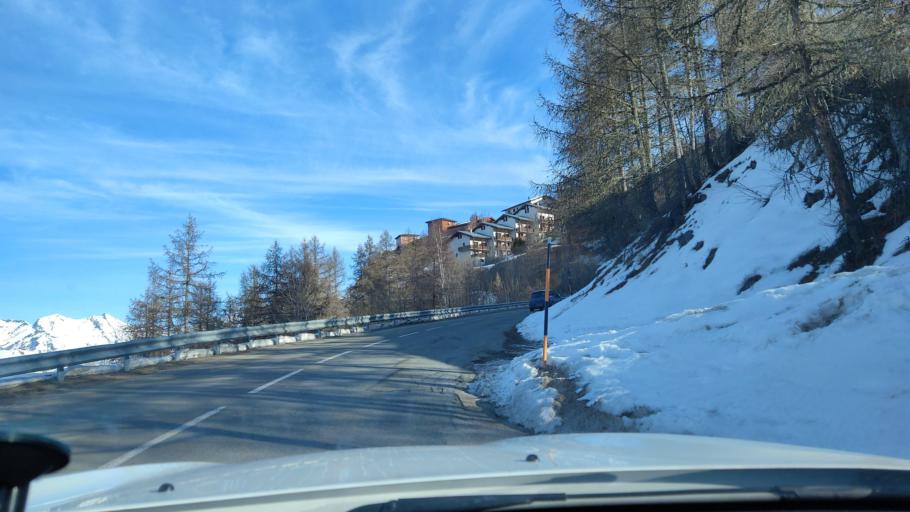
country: FR
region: Rhone-Alpes
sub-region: Departement de la Savoie
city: Bourg-Saint-Maurice
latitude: 45.5506
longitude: 6.7607
